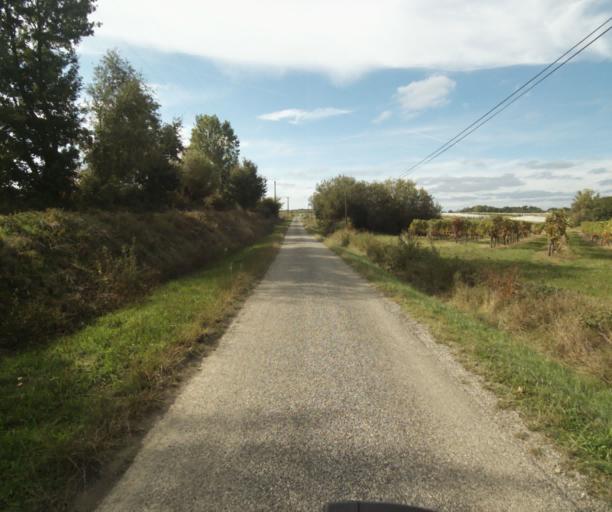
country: FR
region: Midi-Pyrenees
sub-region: Departement du Tarn-et-Garonne
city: Saint-Porquier
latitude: 43.9457
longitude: 1.1362
